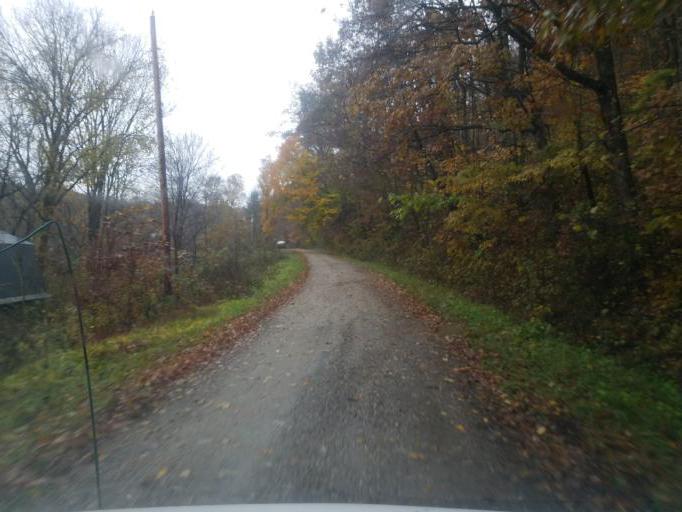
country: US
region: Ohio
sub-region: Washington County
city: Beverly
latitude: 39.4675
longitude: -81.7594
